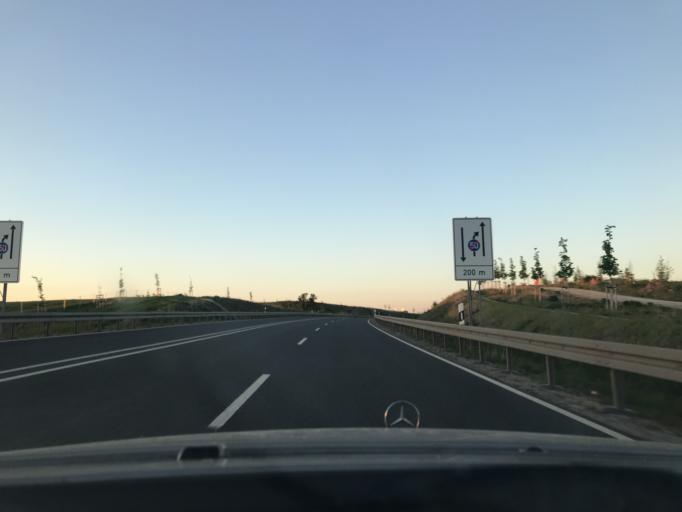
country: DE
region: Thuringia
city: Heilbad Heiligenstadt
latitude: 51.3844
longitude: 10.1160
